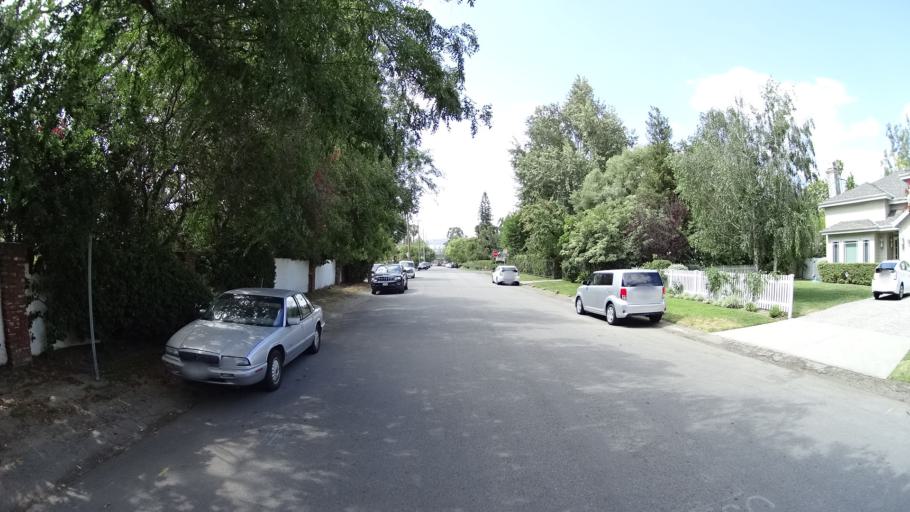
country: US
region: California
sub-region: Los Angeles County
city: Universal City
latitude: 34.1564
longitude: -118.3528
